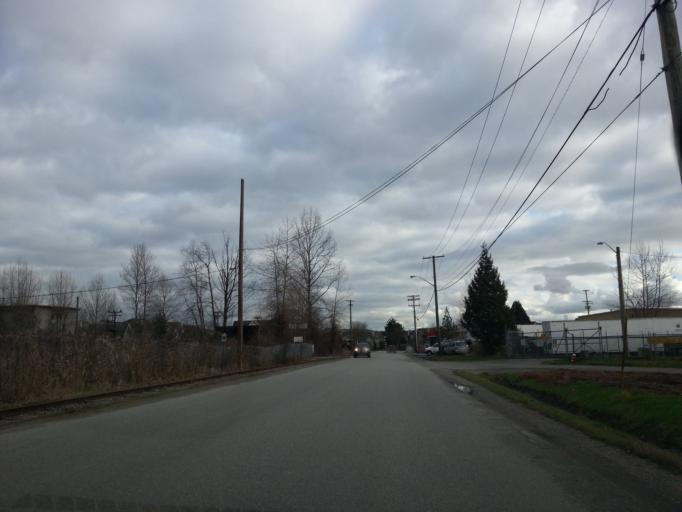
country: CA
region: British Columbia
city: New Westminster
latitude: 49.1949
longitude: -122.9298
